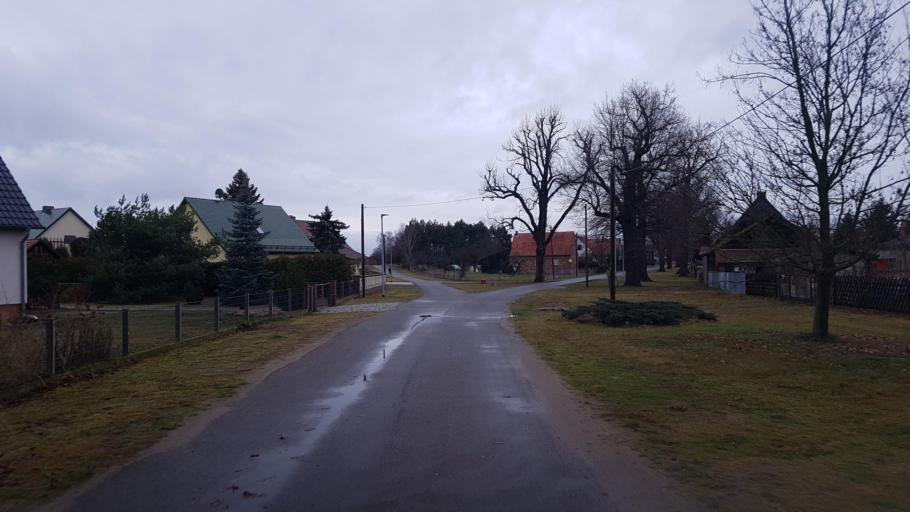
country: DE
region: Brandenburg
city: Tauche
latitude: 52.0686
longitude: 14.0978
